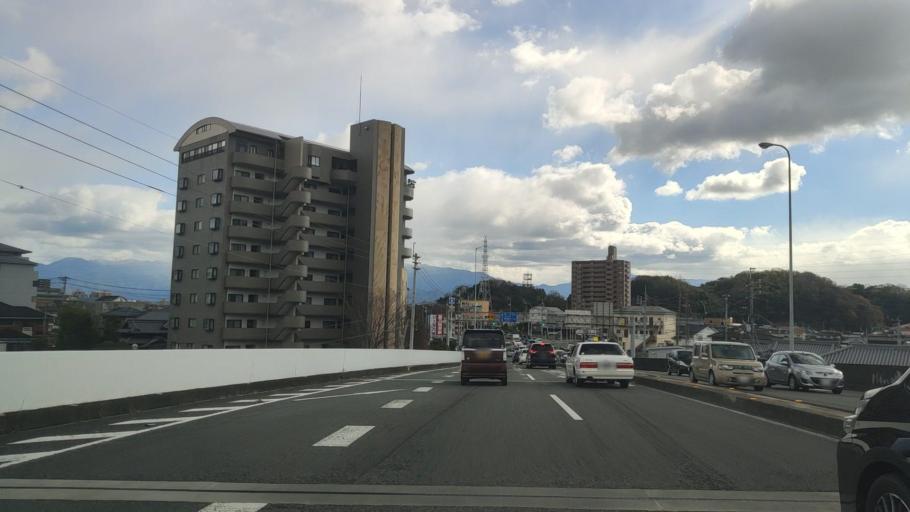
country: JP
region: Ehime
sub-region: Shikoku-chuo Shi
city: Matsuyama
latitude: 33.8232
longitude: 132.7859
